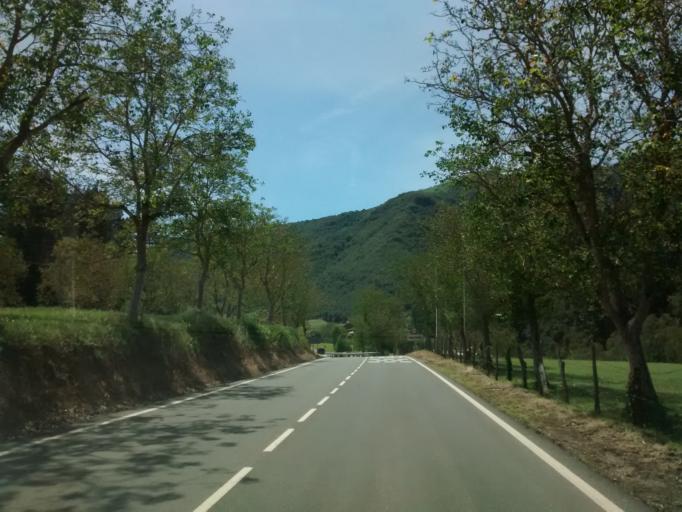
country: ES
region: Cantabria
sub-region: Provincia de Cantabria
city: Potes
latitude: 43.1380
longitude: -4.6289
